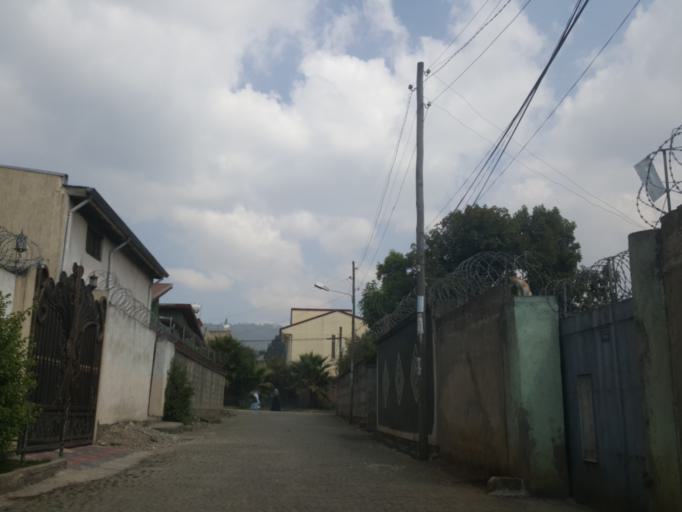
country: ET
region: Adis Abeba
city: Addis Ababa
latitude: 9.0608
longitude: 38.7203
